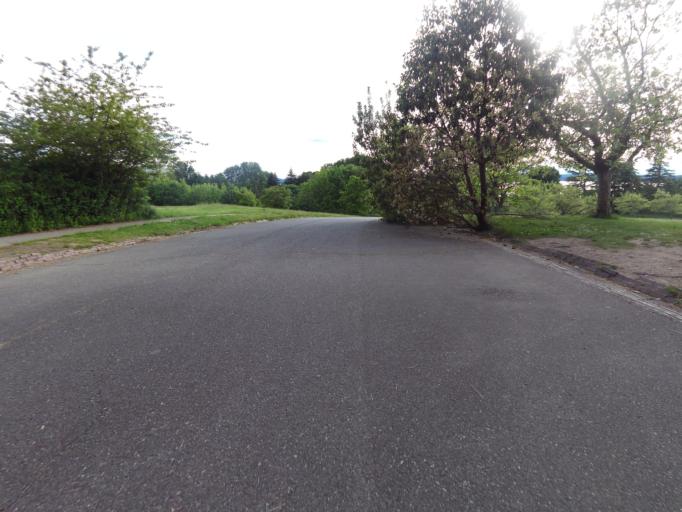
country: US
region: Washington
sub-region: King County
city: Seattle
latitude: 47.6560
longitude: -122.4133
